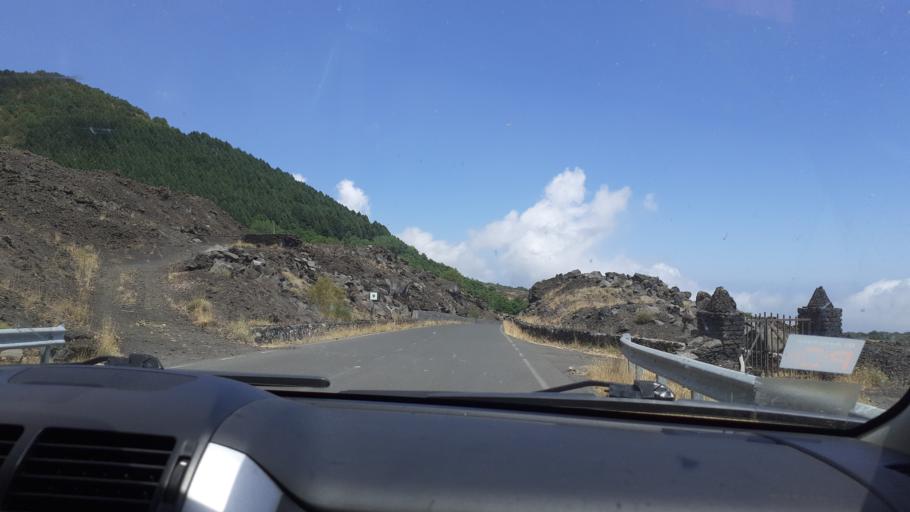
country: IT
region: Sicily
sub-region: Catania
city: Nicolosi
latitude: 37.6867
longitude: 15.0230
